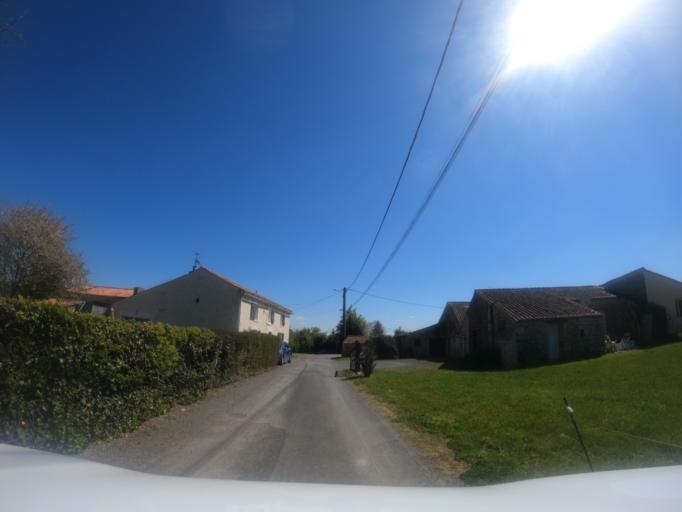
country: FR
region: Pays de la Loire
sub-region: Departement de la Vendee
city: Fontenay-le-Comte
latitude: 46.4435
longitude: -0.8673
